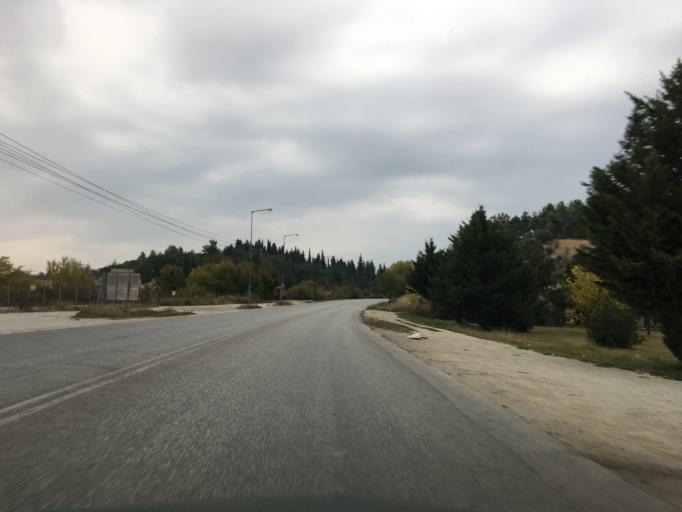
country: GR
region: Thessaly
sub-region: Trikala
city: Trikala
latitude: 39.5698
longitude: 21.7616
